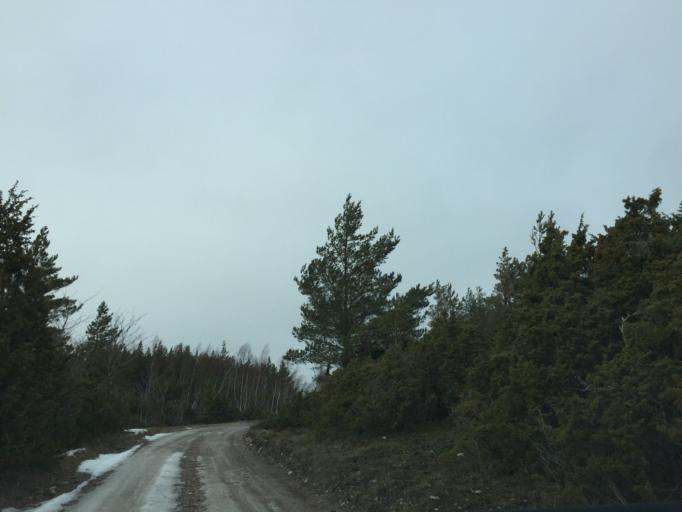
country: EE
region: Saare
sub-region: Kuressaare linn
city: Kuressaare
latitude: 58.4974
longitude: 21.9265
